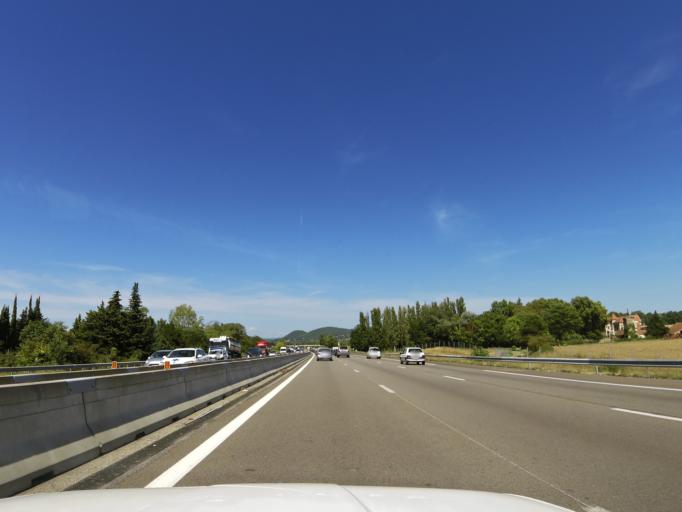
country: FR
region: Rhone-Alpes
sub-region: Departement de la Drome
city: Montboucher-sur-Jabron
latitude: 44.5651
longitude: 4.8106
